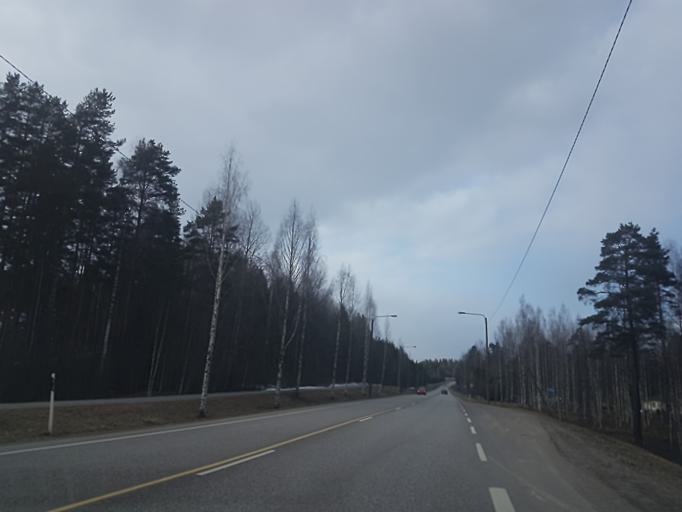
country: FI
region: South Karelia
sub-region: Imatra
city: Parikkala
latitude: 61.5311
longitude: 29.5175
